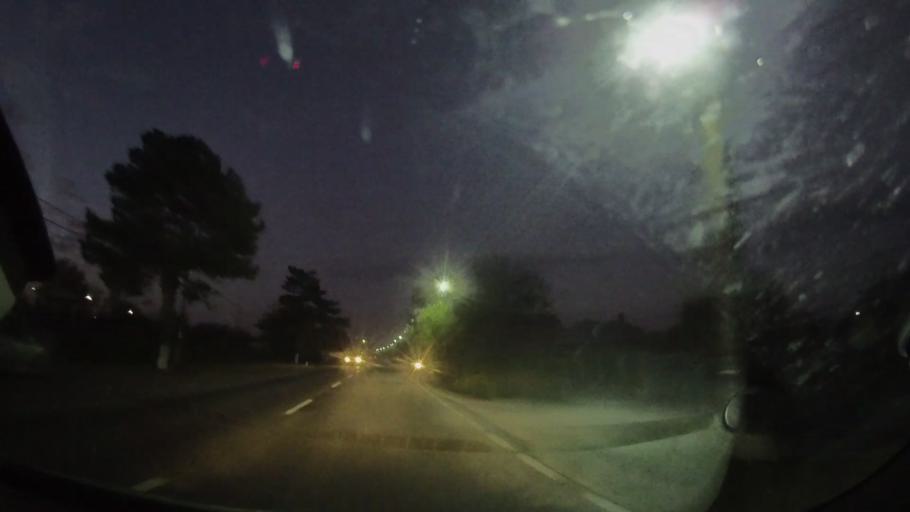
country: RO
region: Tulcea
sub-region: Comuna Mihail Kogalniceanu
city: Mihail Kogalniceanu
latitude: 45.0423
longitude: 28.7353
